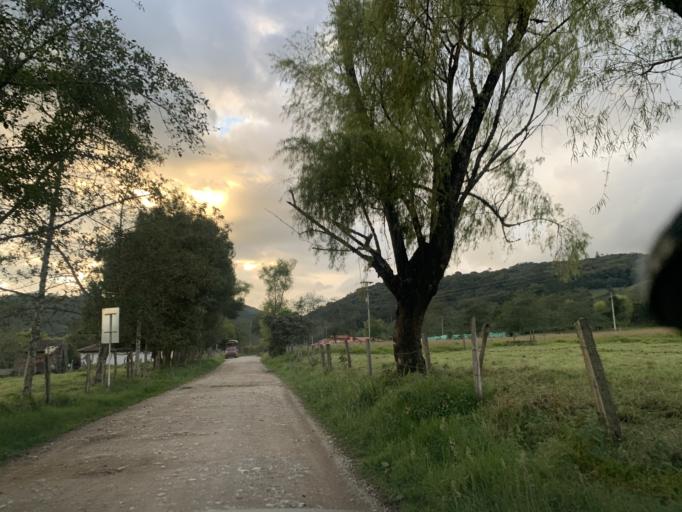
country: CO
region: Boyaca
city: La Capilla
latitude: 5.7376
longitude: -73.5045
